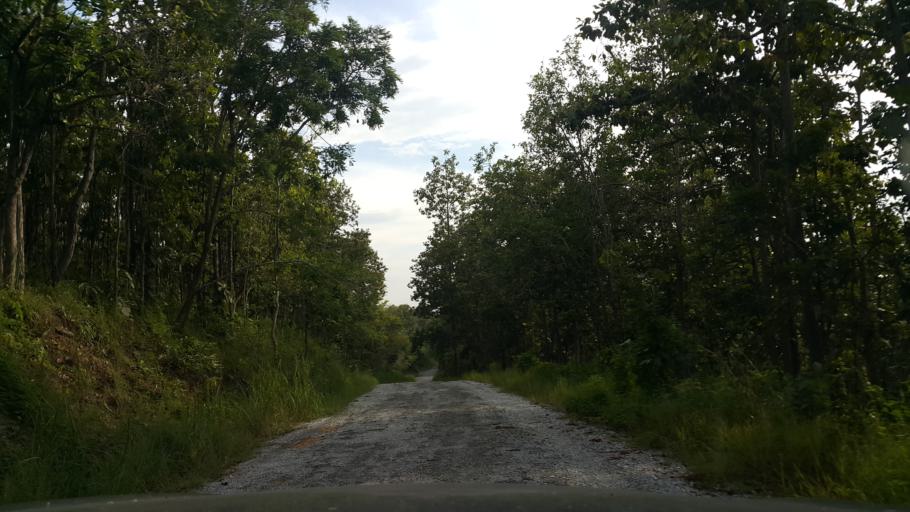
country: TH
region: Chiang Mai
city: San Sai
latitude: 18.9266
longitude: 99.0846
